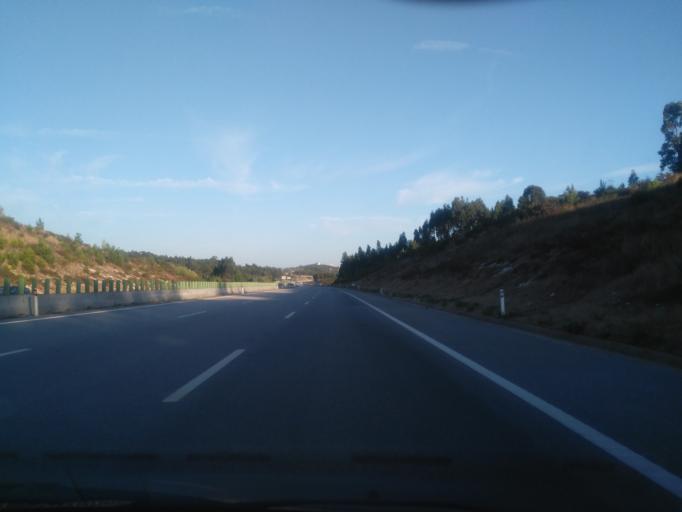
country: PT
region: Coimbra
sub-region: Figueira da Foz
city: Alhadas
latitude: 40.1540
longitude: -8.7695
